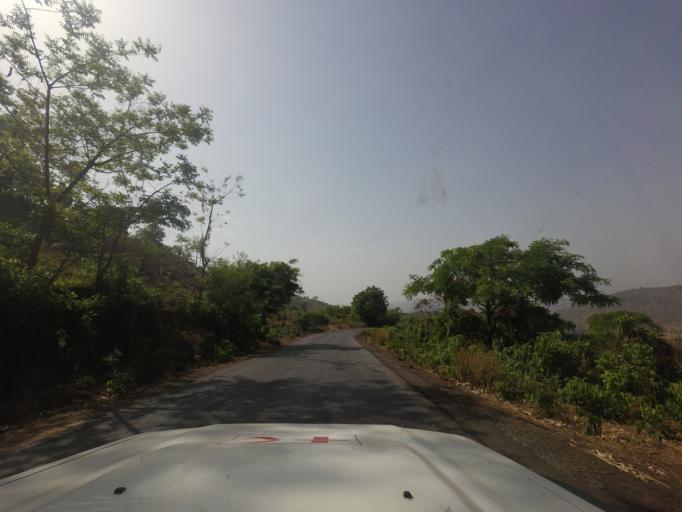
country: GN
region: Mamou
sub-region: Mamou Prefecture
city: Mamou
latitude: 10.2250
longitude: -12.4622
